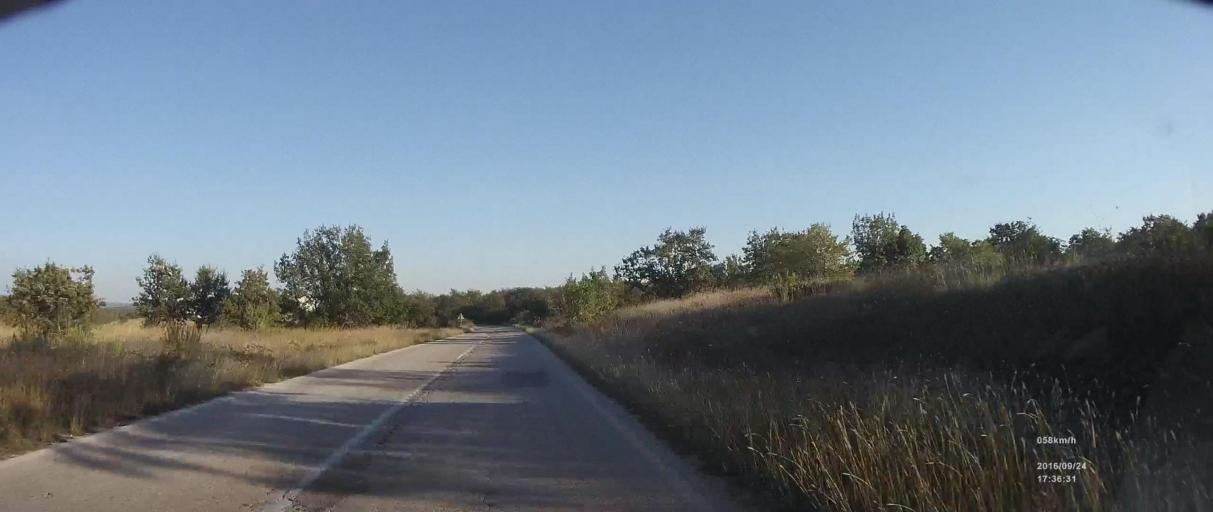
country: HR
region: Zadarska
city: Posedarje
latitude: 44.1545
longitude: 15.4766
